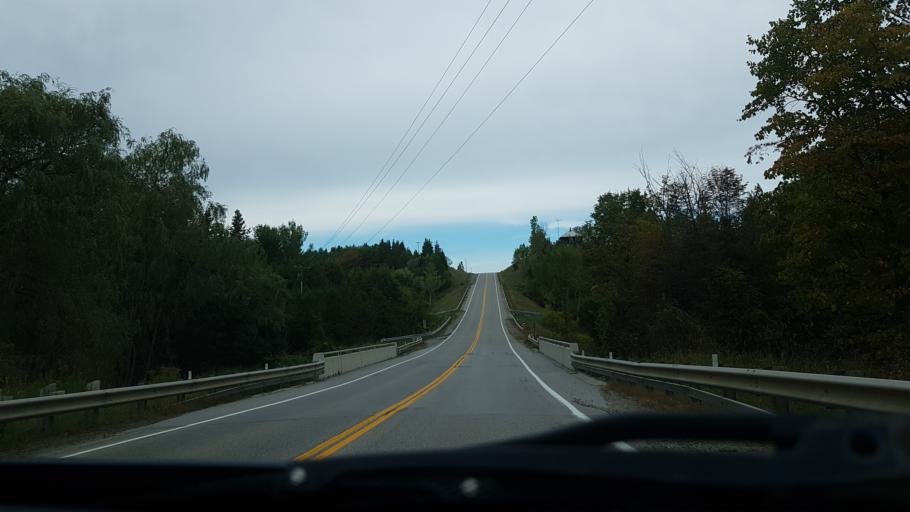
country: CA
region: Ontario
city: Shelburne
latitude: 44.1526
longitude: -80.0341
